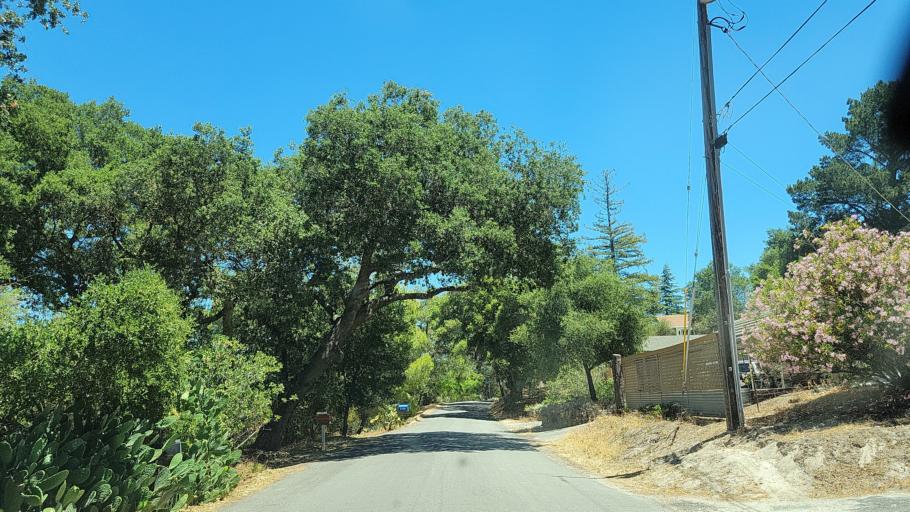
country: US
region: California
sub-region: San Luis Obispo County
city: Atascadero
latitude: 35.4975
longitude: -120.6739
